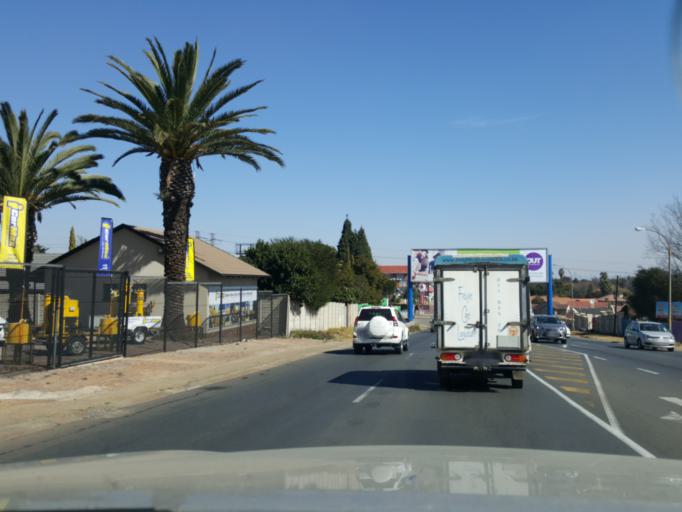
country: ZA
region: Gauteng
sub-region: City of Johannesburg Metropolitan Municipality
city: Modderfontein
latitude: -26.1333
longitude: 28.1981
